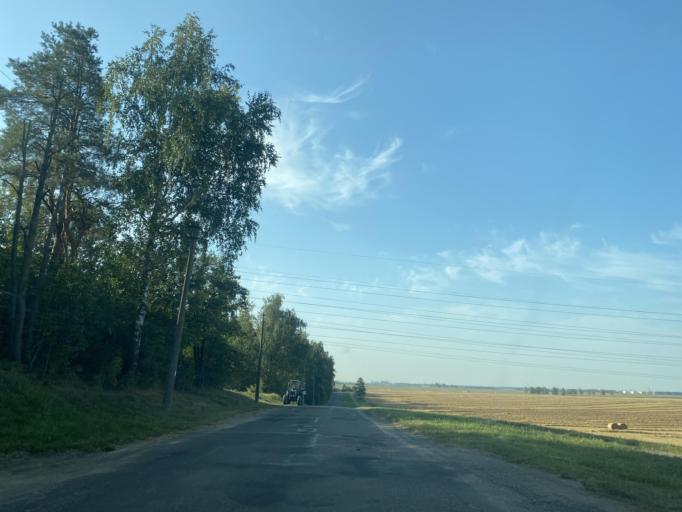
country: BY
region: Minsk
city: Hatava
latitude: 53.8326
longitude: 27.6388
